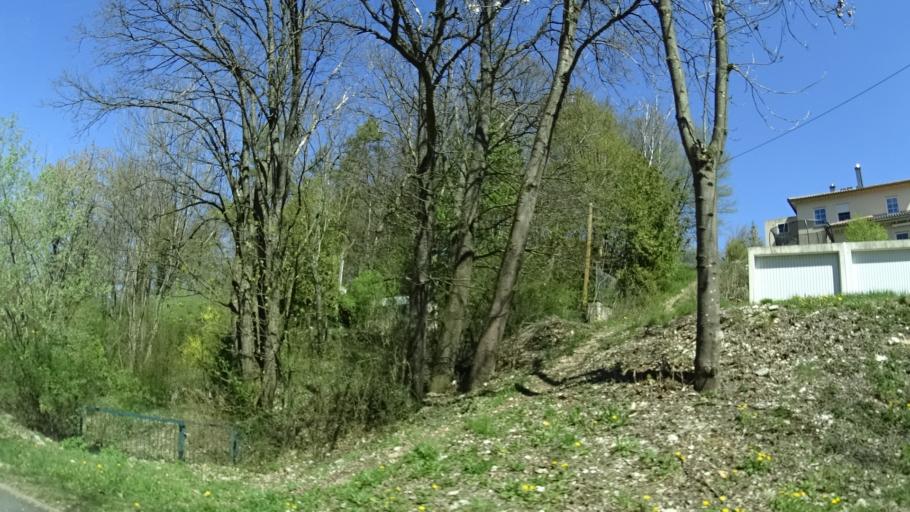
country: DE
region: Bavaria
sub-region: Upper Palatinate
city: Weigendorf
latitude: 49.4958
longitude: 11.5585
